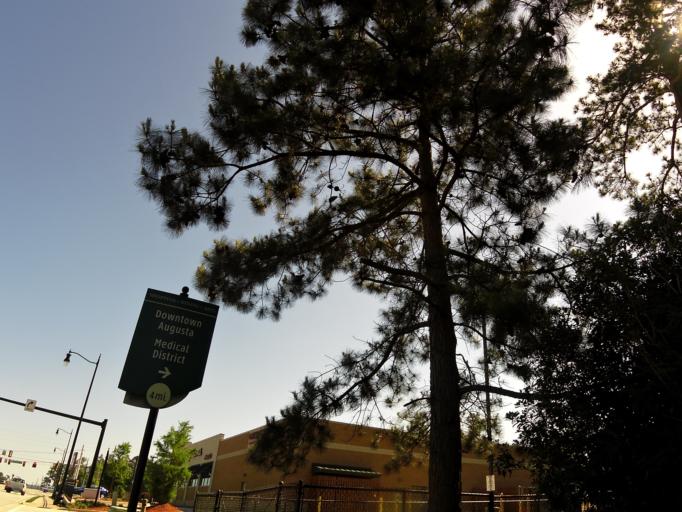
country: US
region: Georgia
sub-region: Columbia County
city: Martinez
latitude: 33.5088
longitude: -82.0287
